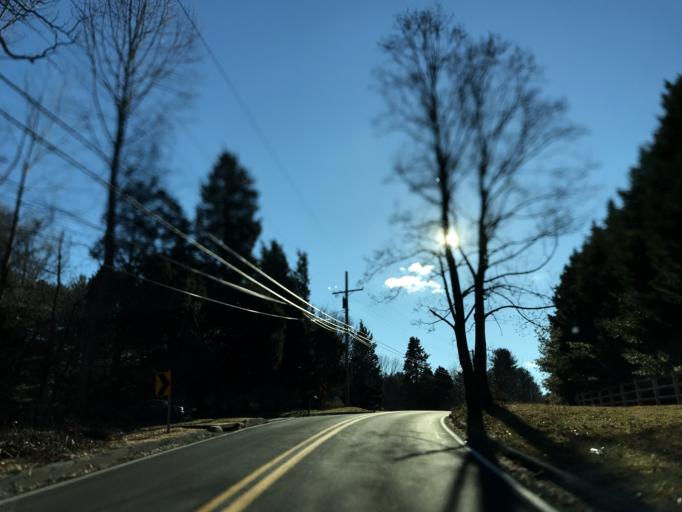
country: US
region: Maryland
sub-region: Howard County
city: Riverside
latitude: 39.1766
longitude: -76.9092
